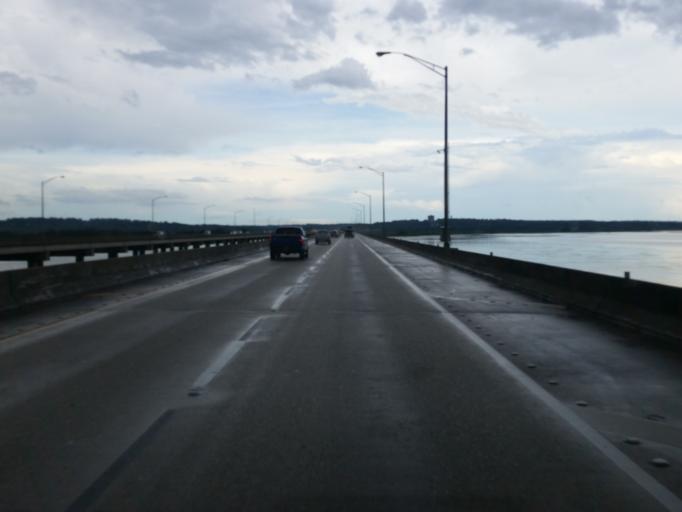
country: US
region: Alabama
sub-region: Baldwin County
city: Spanish Fort
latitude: 30.6601
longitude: -87.9456
